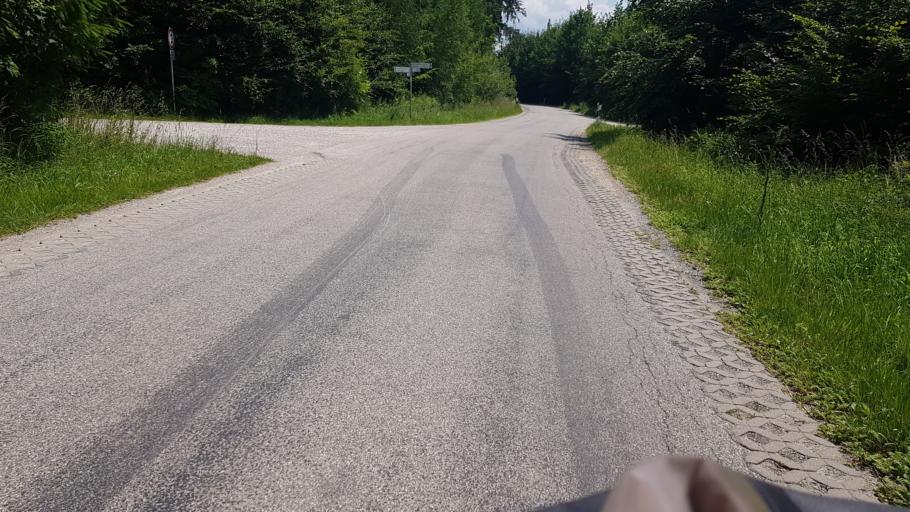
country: DE
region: Bavaria
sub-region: Upper Bavaria
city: Gauting
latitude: 48.0315
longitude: 11.3986
